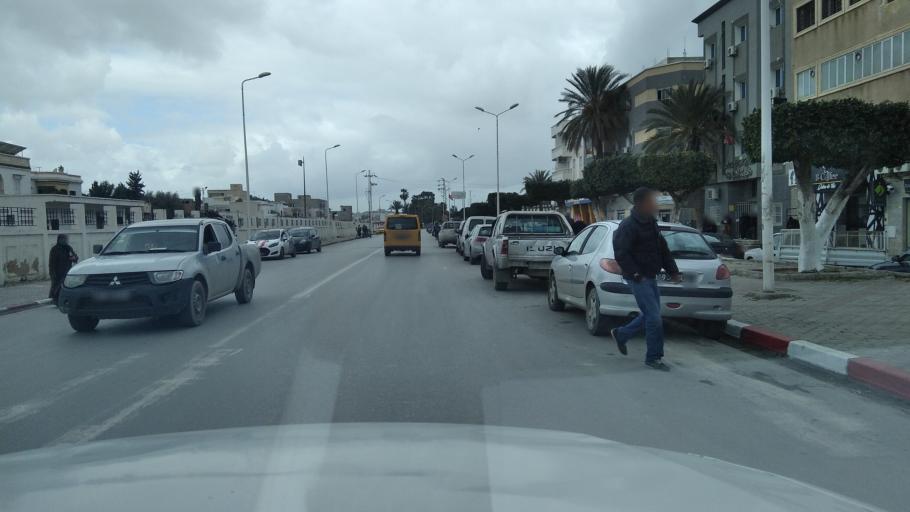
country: TN
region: Bin 'Arus
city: Ben Arous
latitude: 36.7563
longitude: 10.2200
